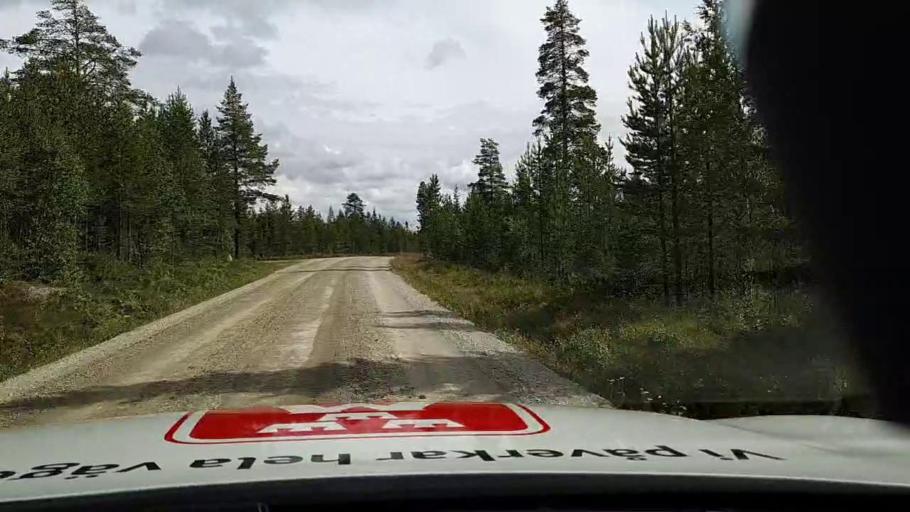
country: SE
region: Jaemtland
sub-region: Are Kommun
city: Jarpen
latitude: 62.5337
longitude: 13.4809
